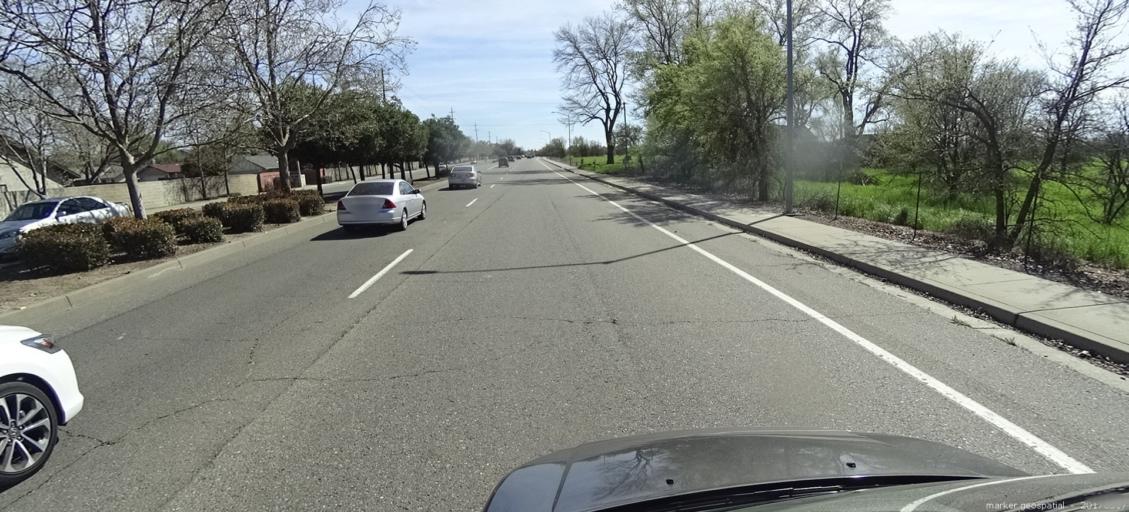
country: US
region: California
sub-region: Sacramento County
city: Parkway
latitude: 38.4591
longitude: -121.4464
